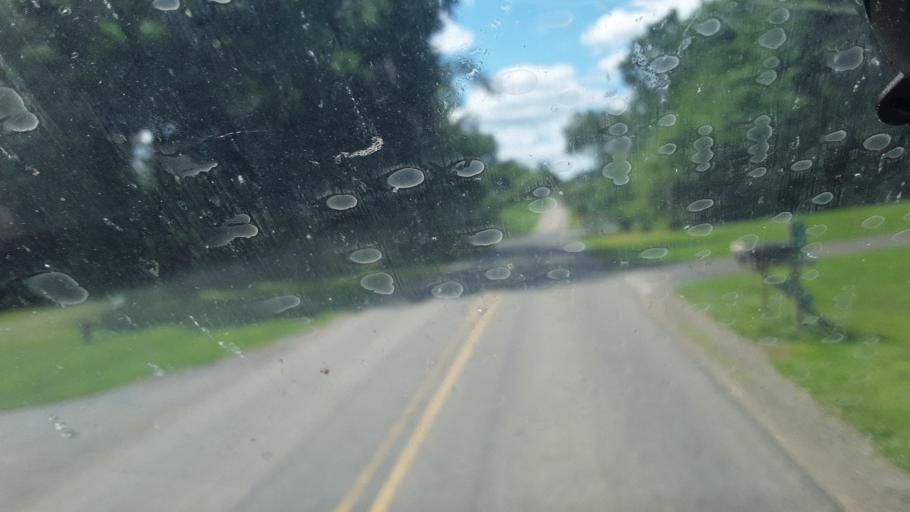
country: US
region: Pennsylvania
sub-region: Lawrence County
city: New Wilmington
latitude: 41.0786
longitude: -80.2636
